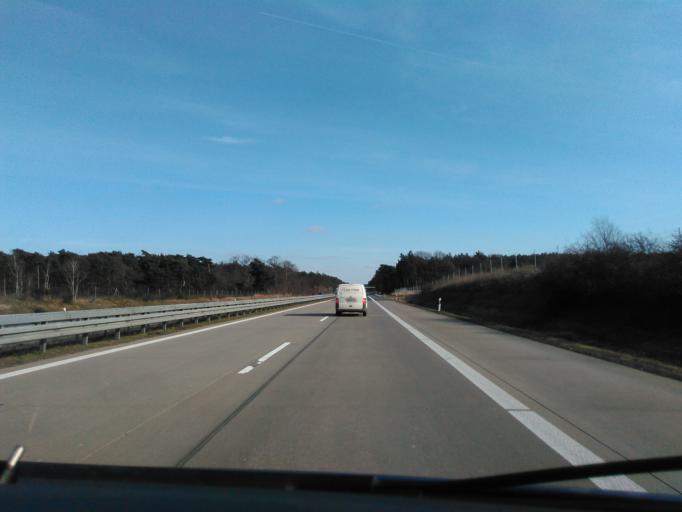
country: DE
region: Brandenburg
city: Luebben
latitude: 51.8858
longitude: 13.8520
